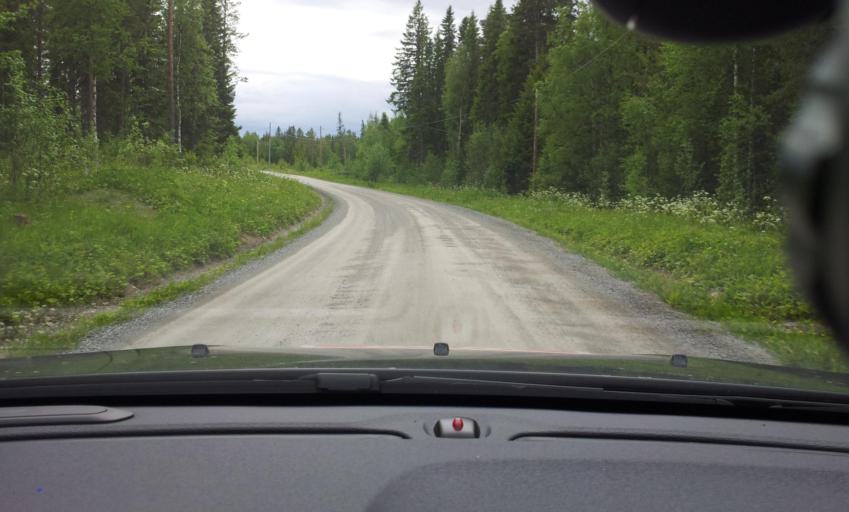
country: SE
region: Jaemtland
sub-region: OEstersunds Kommun
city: Brunflo
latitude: 62.9882
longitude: 14.7146
